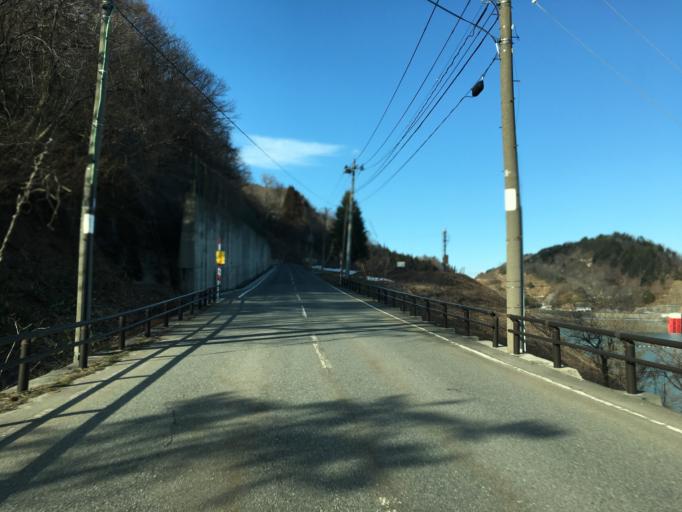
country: JP
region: Yamagata
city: Nagai
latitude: 37.9705
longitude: 139.9159
